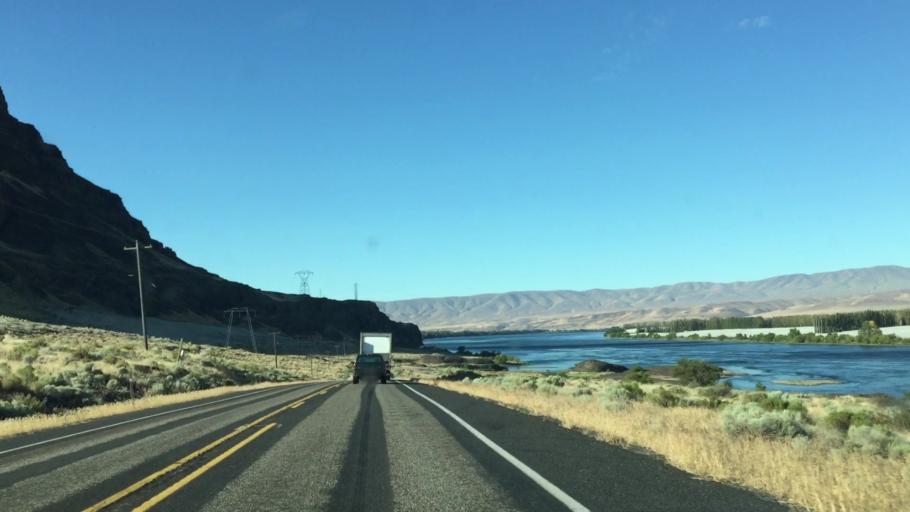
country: US
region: Washington
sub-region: Grant County
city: Mattawa
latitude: 46.8096
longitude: -119.9207
